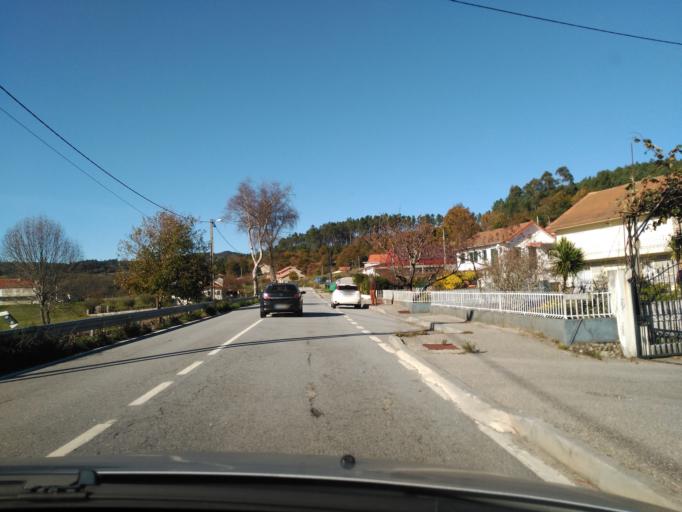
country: PT
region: Braga
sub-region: Cabeceiras de Basto
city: Cabeceiras de Basto
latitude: 41.6809
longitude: -7.9509
